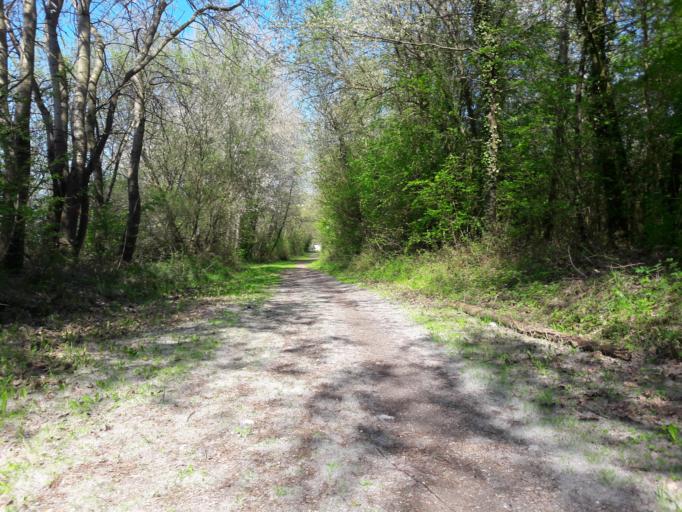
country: FR
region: Nord-Pas-de-Calais
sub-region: Departement du Nord
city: Sains-du-Nord
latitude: 50.1697
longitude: 4.0766
